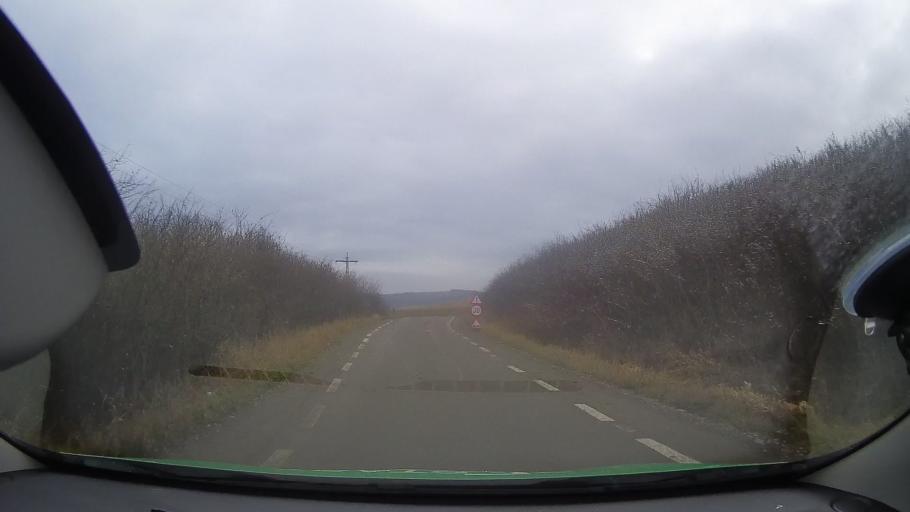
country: RO
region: Mures
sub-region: Comuna Atintis
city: Atintis
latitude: 46.4067
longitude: 24.0863
